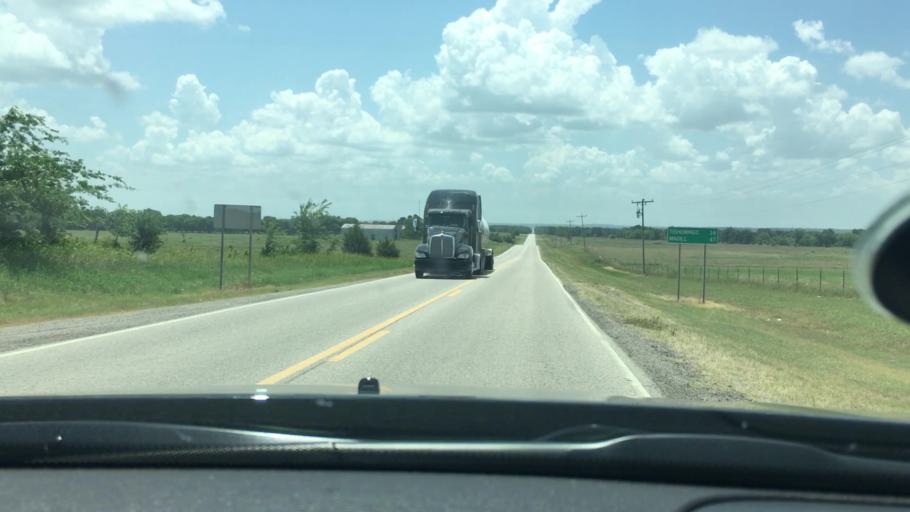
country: US
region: Oklahoma
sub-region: Pontotoc County
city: Ada
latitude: 34.7233
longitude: -96.6349
